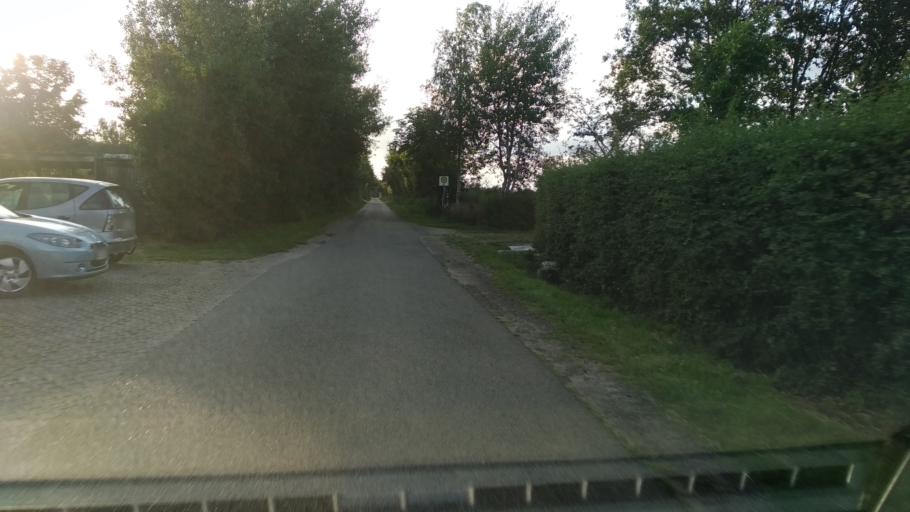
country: DE
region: Schleswig-Holstein
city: Borm
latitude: 54.4144
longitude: 9.4059
